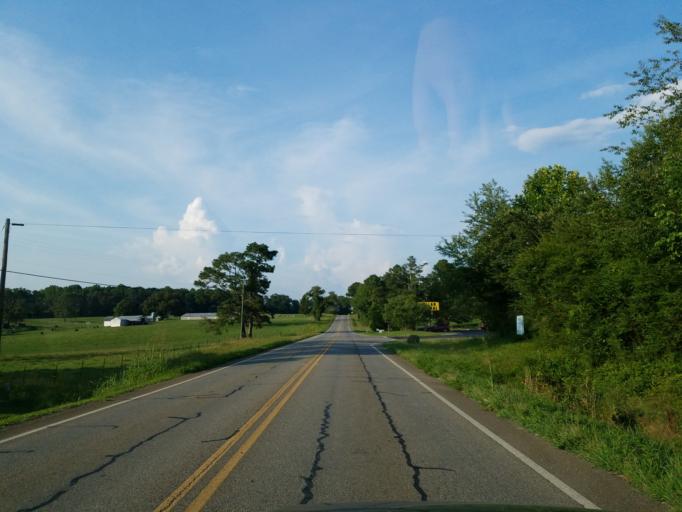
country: US
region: Georgia
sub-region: Pickens County
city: Jasper
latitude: 34.4833
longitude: -84.5817
